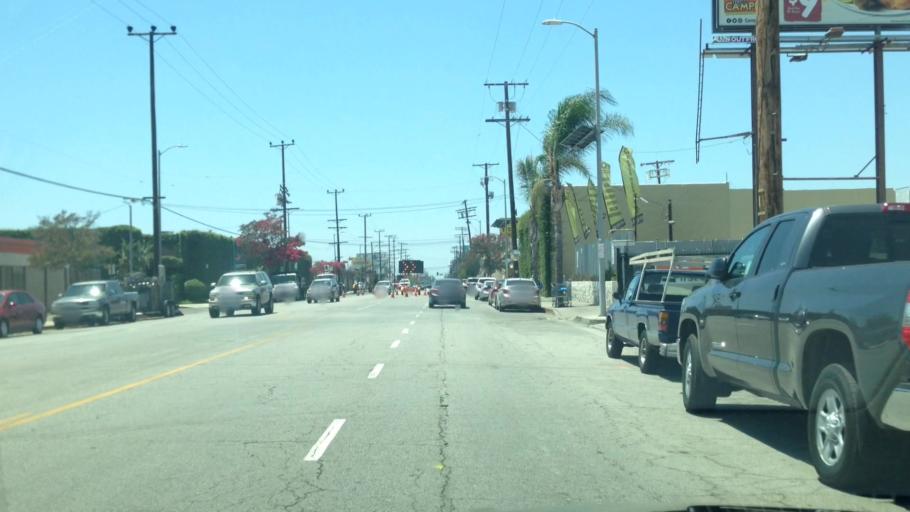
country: US
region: California
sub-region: Los Angeles County
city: North Hollywood
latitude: 34.1940
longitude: -118.3663
